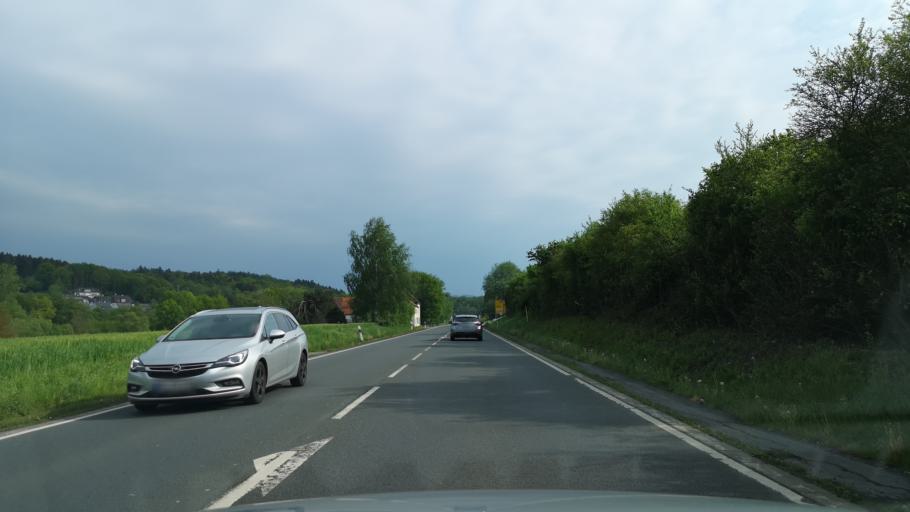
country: DE
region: North Rhine-Westphalia
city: Iserlohn
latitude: 51.4169
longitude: 7.6914
